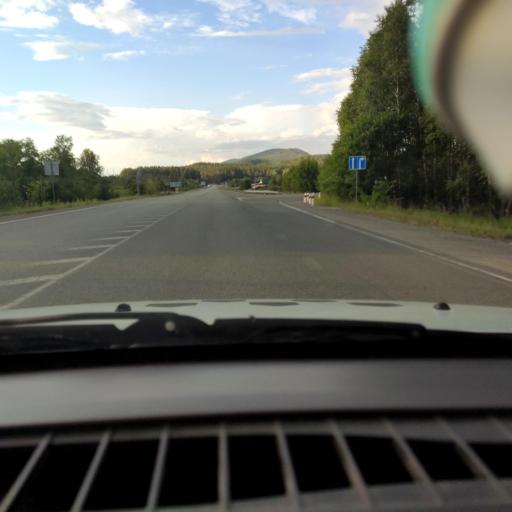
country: RU
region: Chelyabinsk
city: Turgoyak
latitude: 55.2241
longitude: 60.1868
